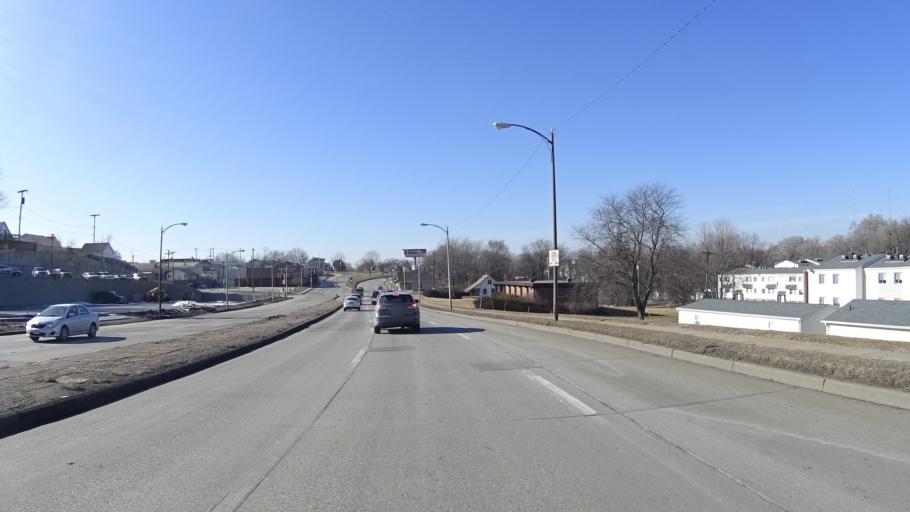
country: US
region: Nebraska
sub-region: Douglas County
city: Omaha
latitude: 41.2869
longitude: -96.0054
